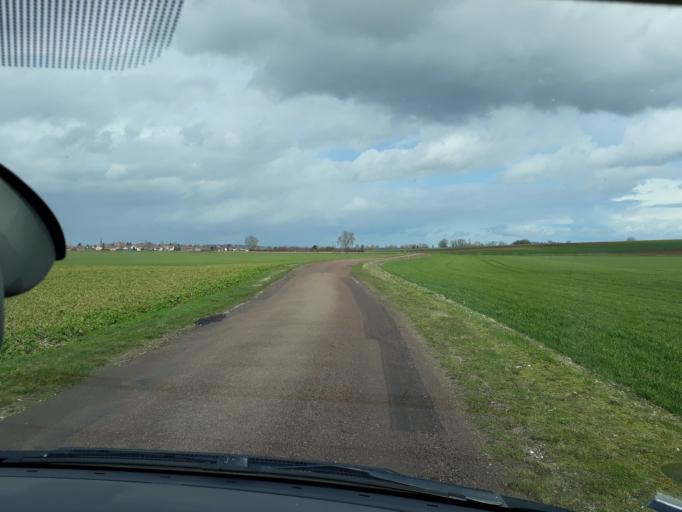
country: FR
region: Bourgogne
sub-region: Departement de la Cote-d'Or
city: Longecourt-en-Plaine
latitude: 47.2141
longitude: 5.1900
